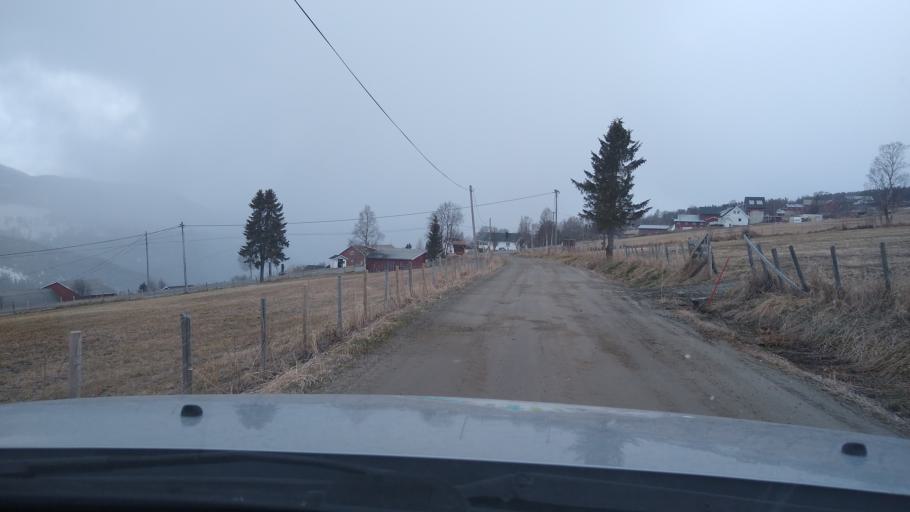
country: NO
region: Oppland
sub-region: Oyer
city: Tretten
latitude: 61.4604
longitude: 10.3300
